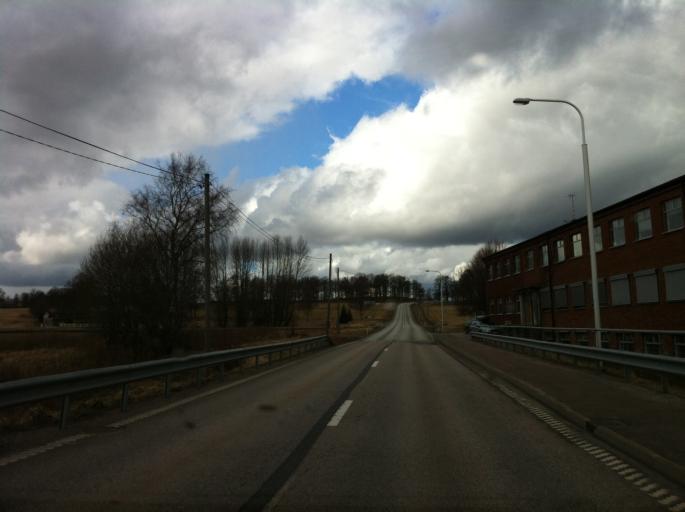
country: SE
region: Vaestra Goetaland
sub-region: Ulricehamns Kommun
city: Ulricehamn
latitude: 57.6526
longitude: 13.4366
